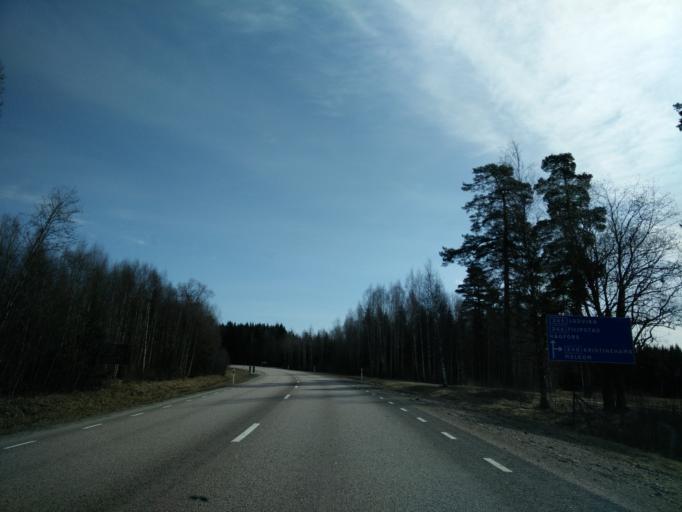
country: SE
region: Vaermland
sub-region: Hagfors Kommun
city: Hagfors
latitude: 60.0098
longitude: 13.6379
